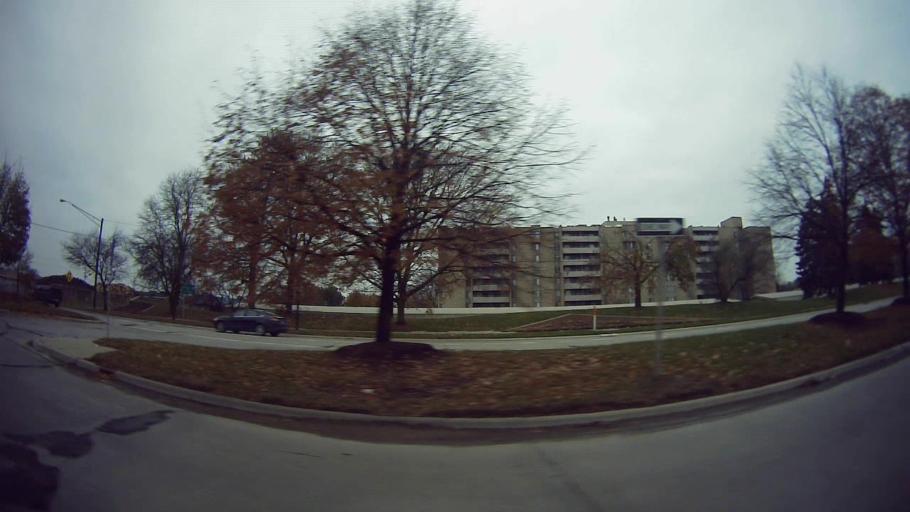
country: US
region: Michigan
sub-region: Oakland County
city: Southfield
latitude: 42.4459
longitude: -83.2590
